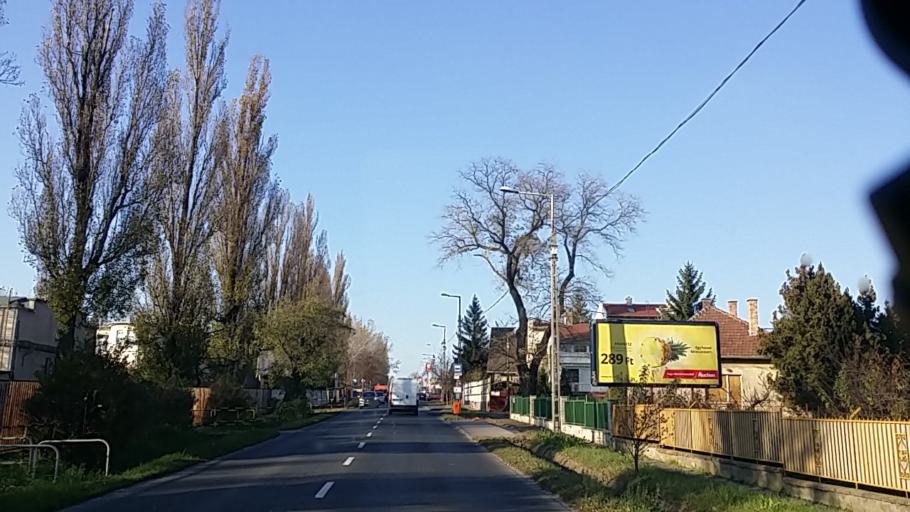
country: HU
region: Budapest
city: Budapest XVII. keruelet
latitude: 47.4902
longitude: 19.2437
